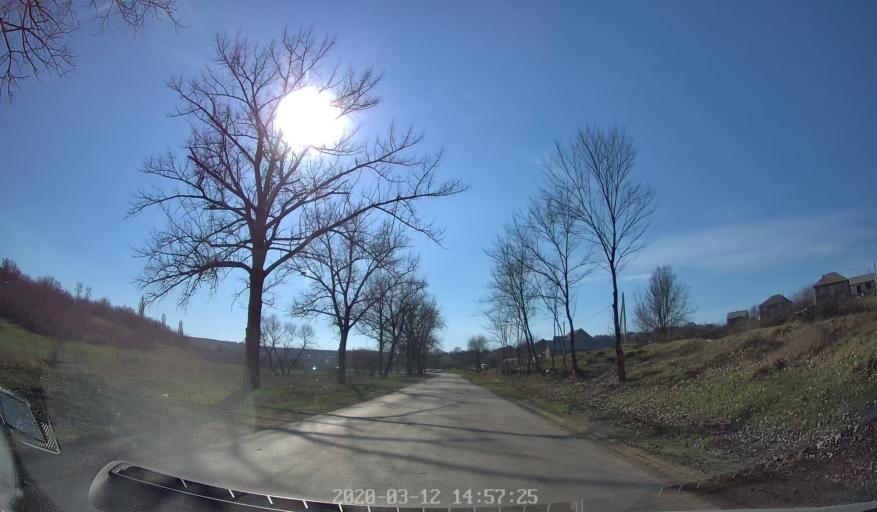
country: MD
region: Telenesti
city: Cocieri
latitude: 47.2237
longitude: 29.0386
